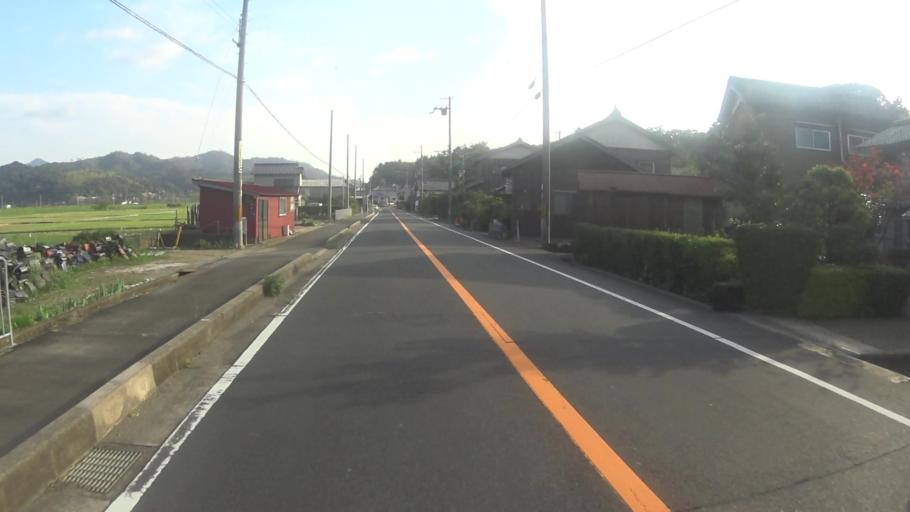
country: JP
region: Kyoto
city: Miyazu
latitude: 35.7194
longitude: 135.1045
